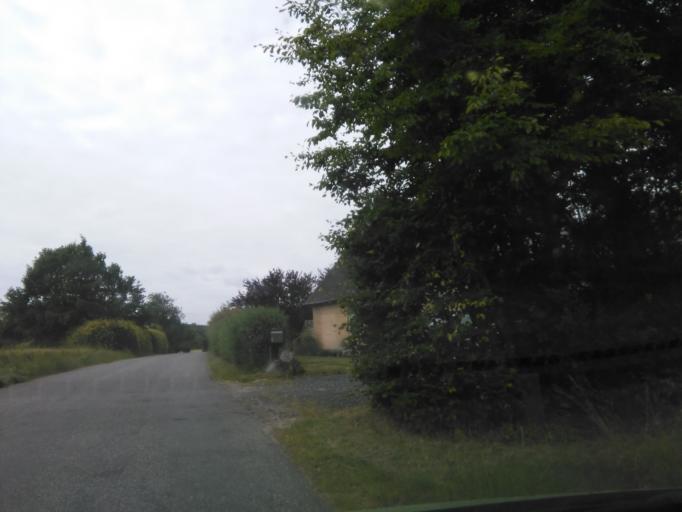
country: DK
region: Central Jutland
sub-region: Arhus Kommune
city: Solbjerg
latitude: 56.0166
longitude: 10.0712
